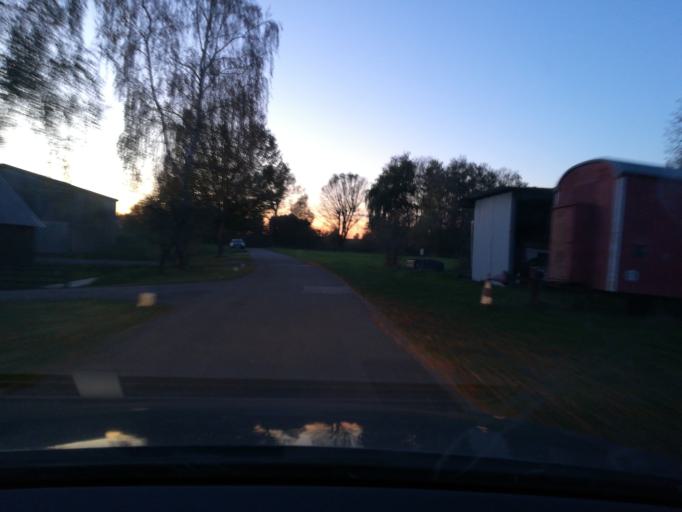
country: DE
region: Lower Saxony
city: Winsen
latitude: 53.4043
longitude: 10.1967
